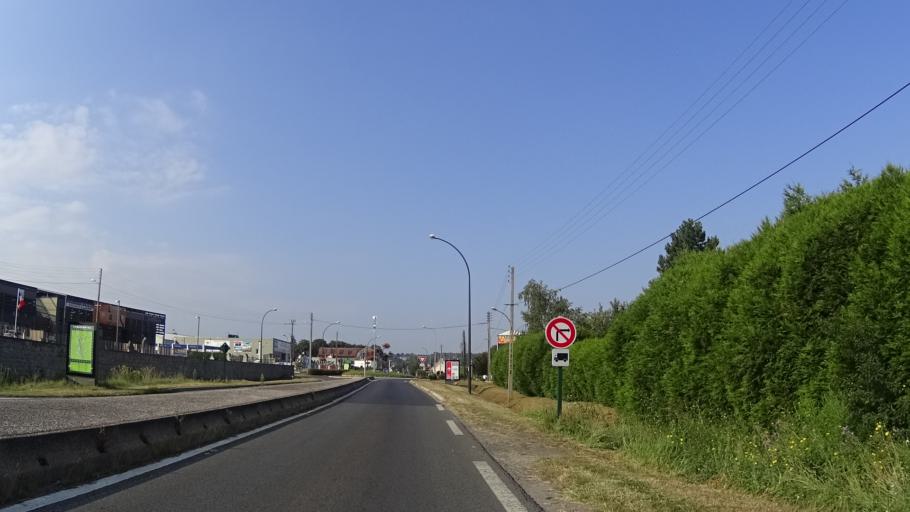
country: FR
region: Ile-de-France
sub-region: Departement du Val-d'Oise
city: Chaumontel
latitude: 49.1277
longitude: 2.4303
